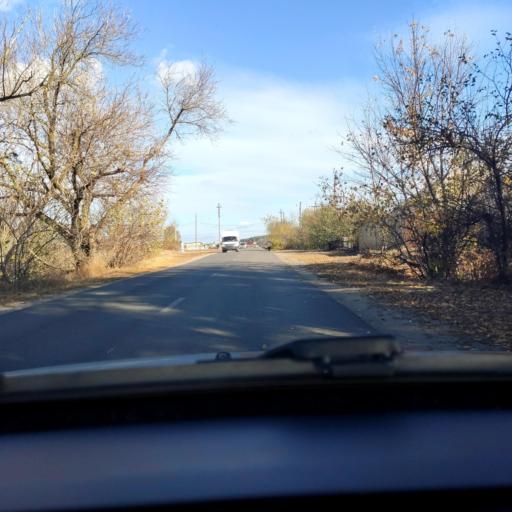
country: RU
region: Voronezj
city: Shilovo
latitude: 51.5261
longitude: 39.1510
